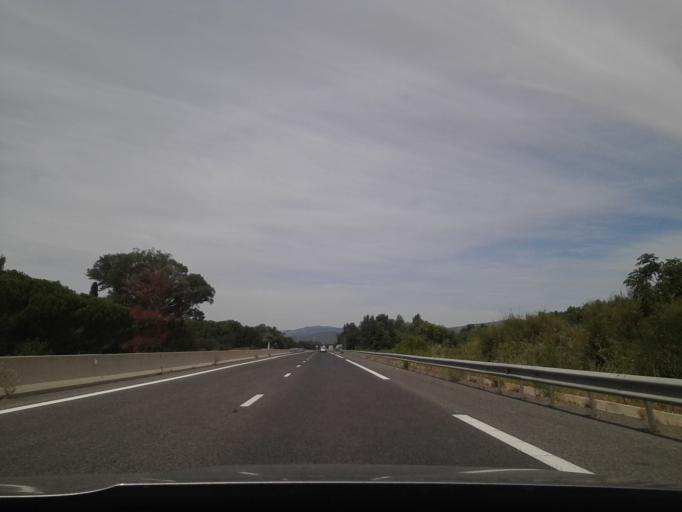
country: FR
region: Languedoc-Roussillon
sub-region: Departement des Pyrenees-Orientales
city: Corneilla-la-Riviere
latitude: 42.6896
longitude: 2.7258
